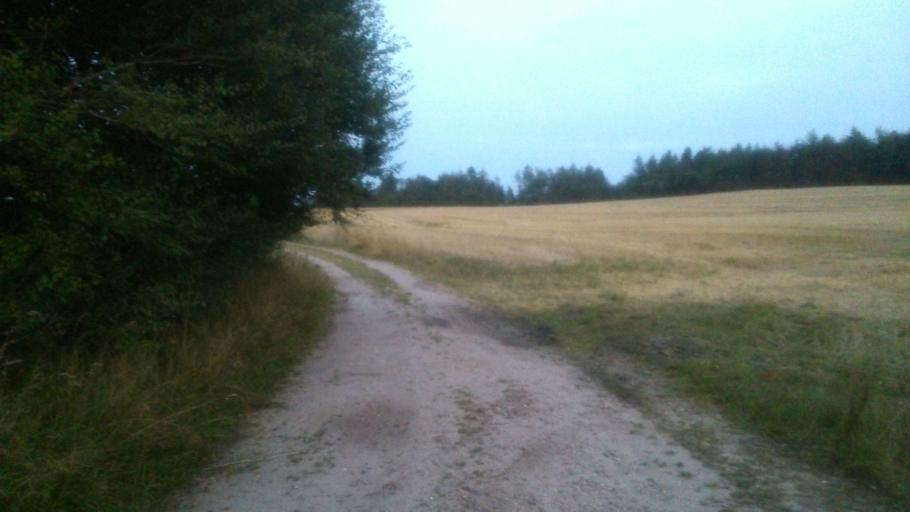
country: DK
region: Central Jutland
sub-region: Ringkobing-Skjern Kommune
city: Skjern
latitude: 56.0051
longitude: 8.4689
